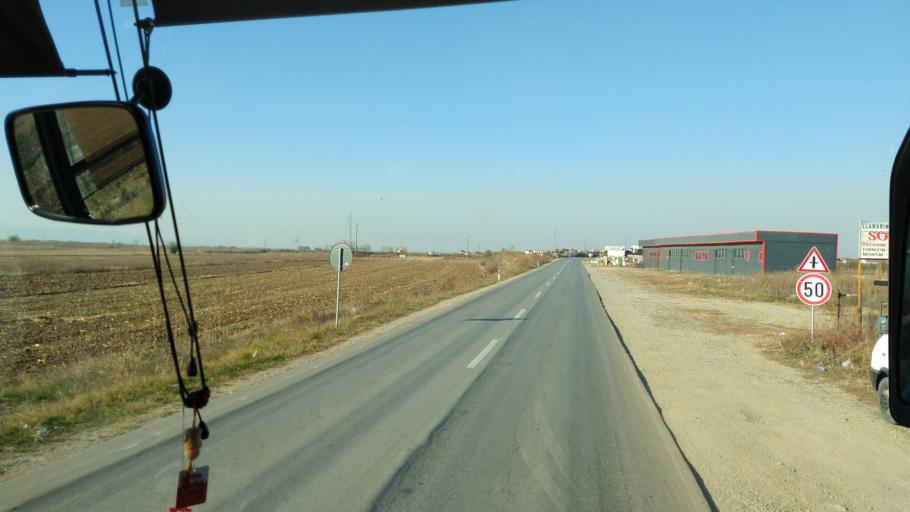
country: XK
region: Pristina
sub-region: Lipjan
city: Lipljan
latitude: 42.5233
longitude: 21.1123
